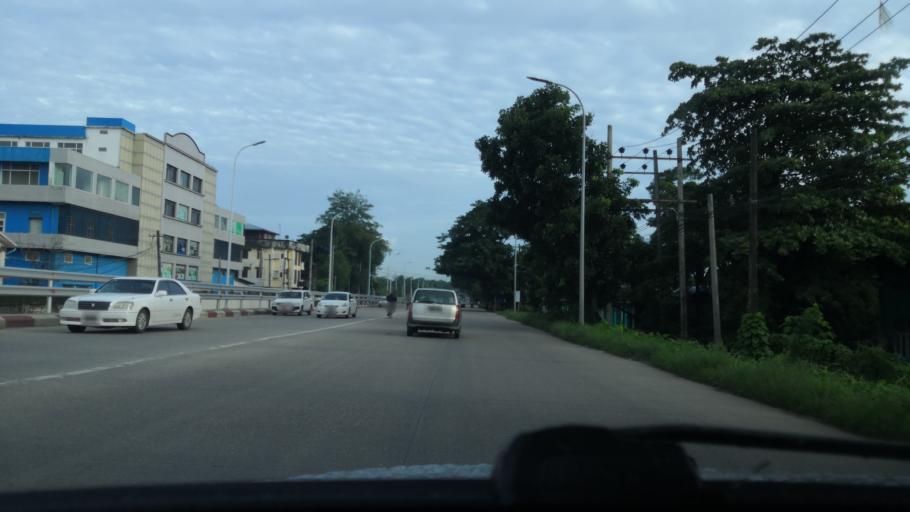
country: MM
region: Yangon
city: Yangon
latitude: 16.8909
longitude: 96.1602
